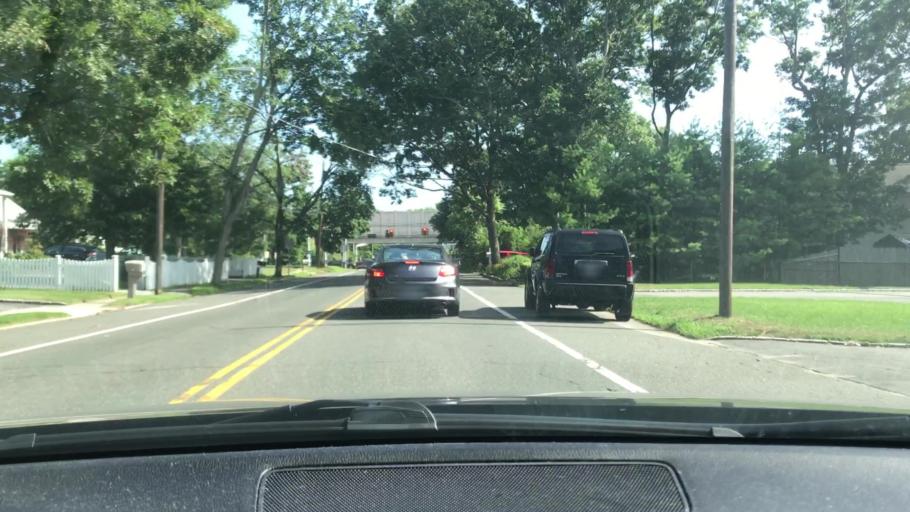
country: US
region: New York
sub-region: Suffolk County
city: Holbrook
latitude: 40.8178
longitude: -73.0794
